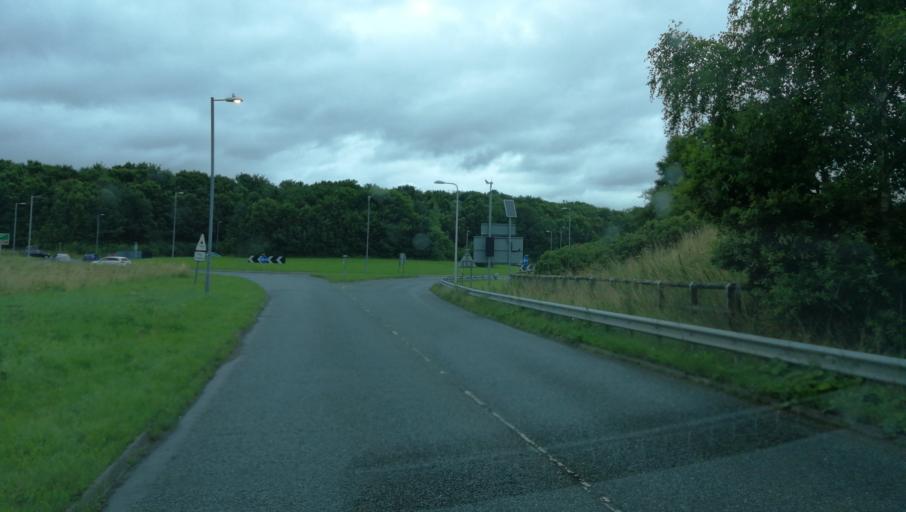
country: GB
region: England
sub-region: Cumbria
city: Penrith
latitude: 54.6473
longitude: -2.7818
